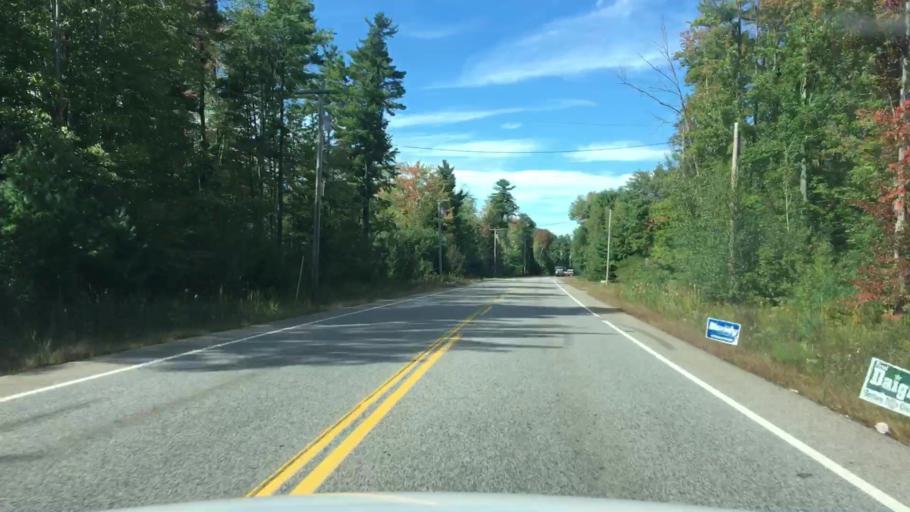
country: US
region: Maine
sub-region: Cumberland County
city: Westbrook
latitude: 43.6516
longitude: -70.3978
